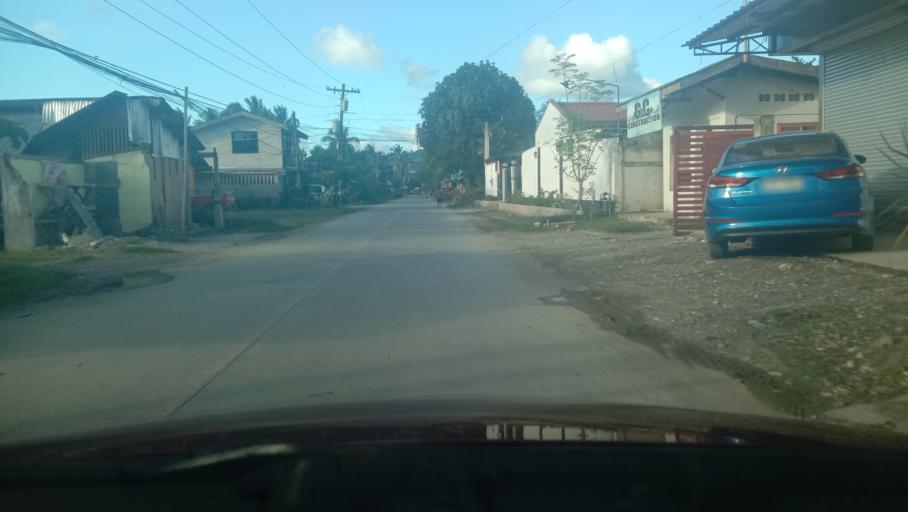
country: PH
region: Caraga
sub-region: Province of Agusan del Sur
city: San Francisco
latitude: 8.5107
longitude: 125.9731
